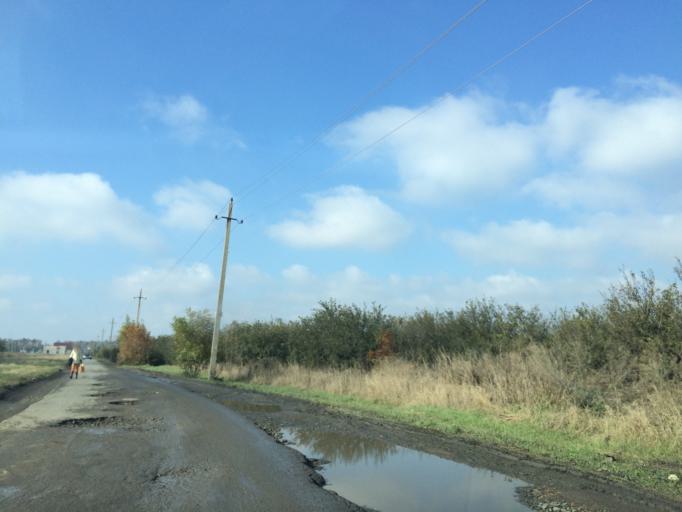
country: RU
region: Rostov
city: Aksay
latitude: 47.2920
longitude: 39.8428
